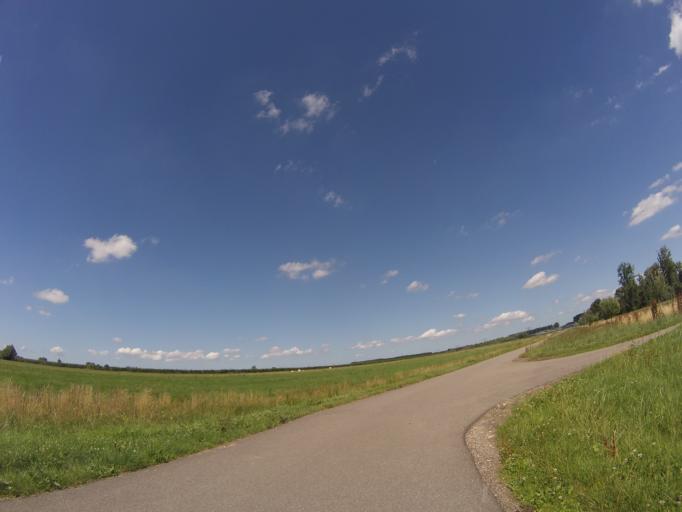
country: NL
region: Utrecht
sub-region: Stichtse Vecht
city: Spechtenkamp
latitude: 52.1307
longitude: 5.0030
